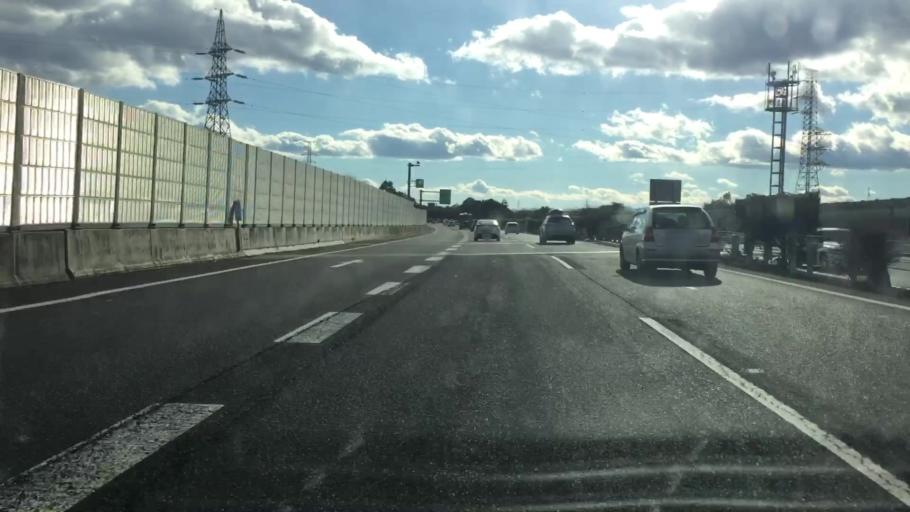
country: JP
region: Gunma
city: Shibukawa
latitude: 36.4701
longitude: 139.0125
